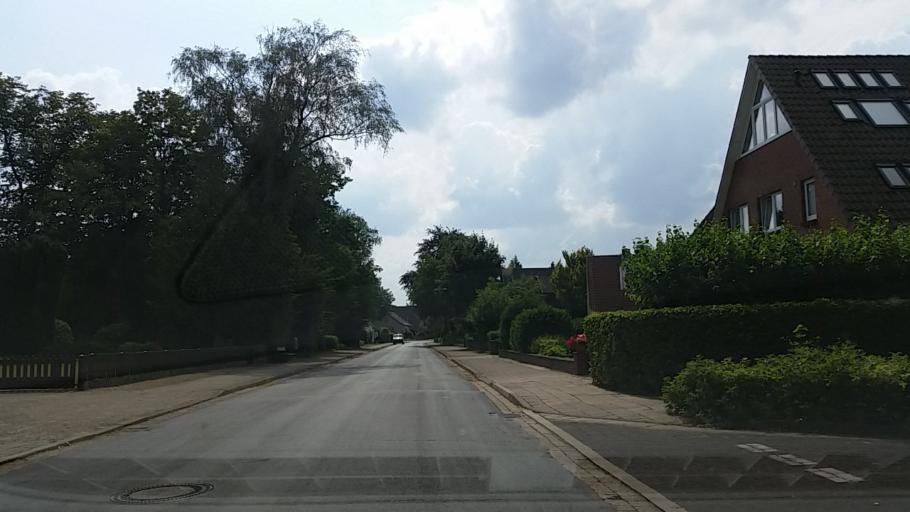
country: DE
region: Lower Saxony
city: Schneverdingen
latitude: 53.1235
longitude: 9.7855
